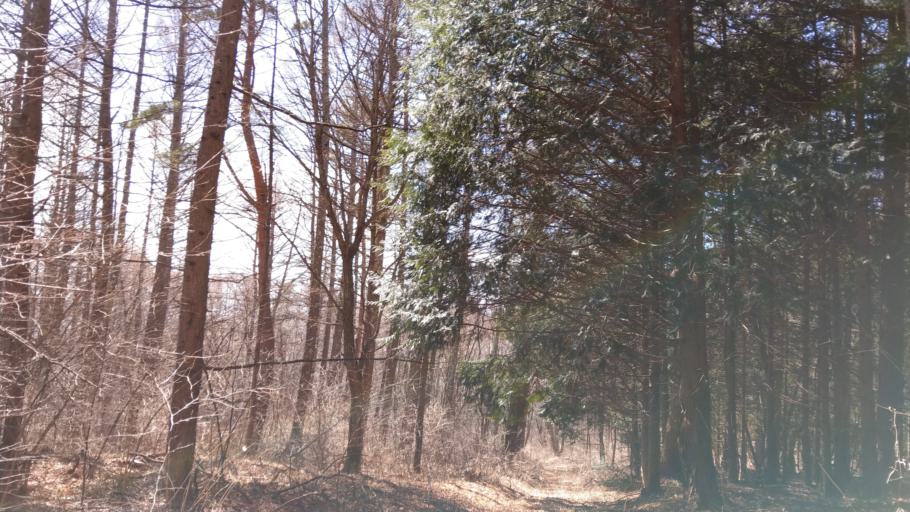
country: JP
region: Nagano
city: Komoro
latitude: 36.3719
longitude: 138.4294
